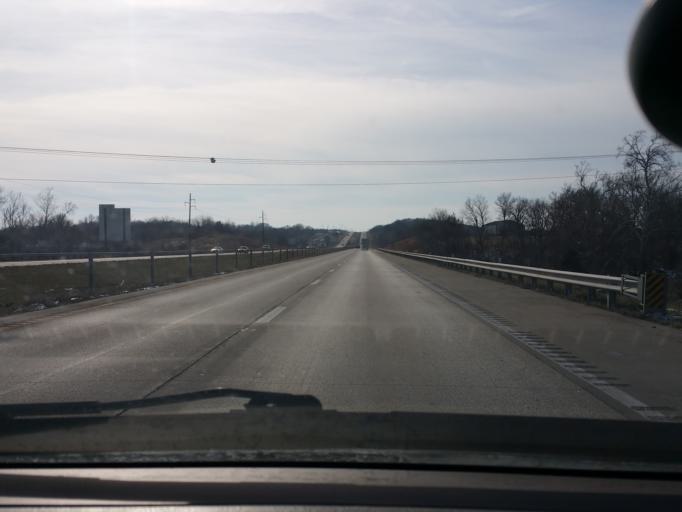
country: US
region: Missouri
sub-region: Clay County
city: Kearney
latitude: 39.3538
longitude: -94.3800
